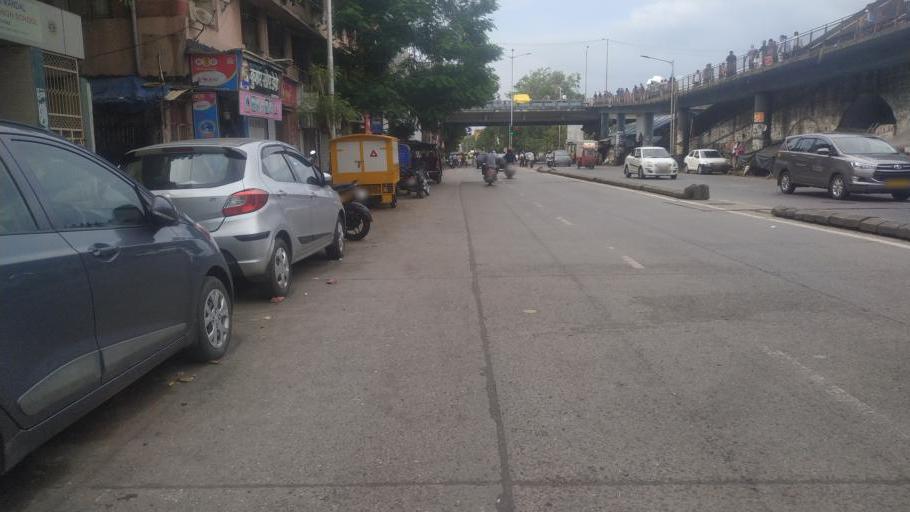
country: IN
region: Maharashtra
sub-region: Mumbai Suburban
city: Mumbai
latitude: 19.0296
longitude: 72.8469
